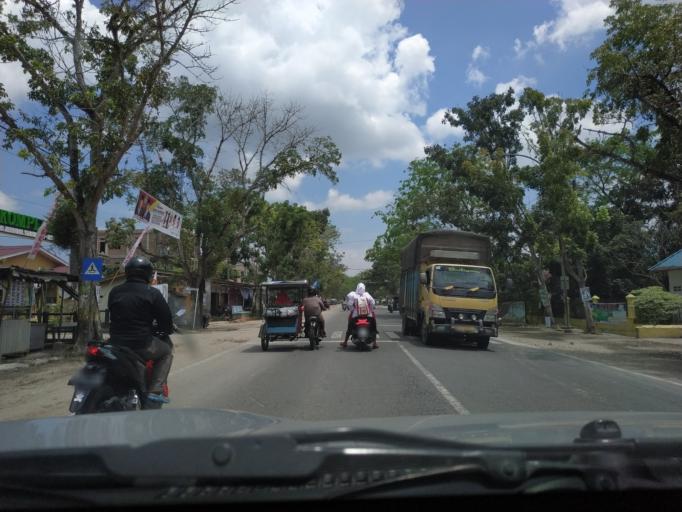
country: ID
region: North Sumatra
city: Tanjungbalai
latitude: 2.9489
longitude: 99.7751
